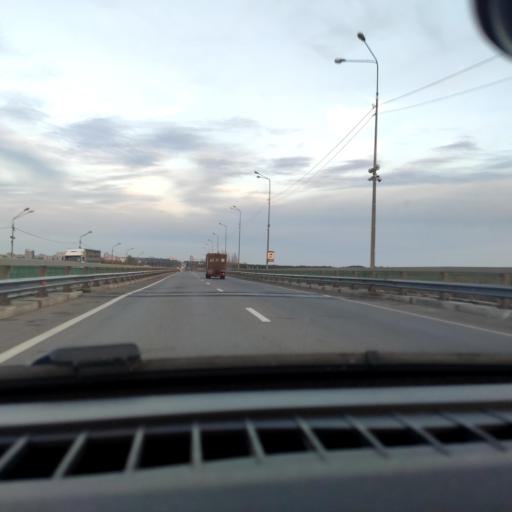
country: RU
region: Voronezj
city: Pridonskoy
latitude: 51.6510
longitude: 39.0657
